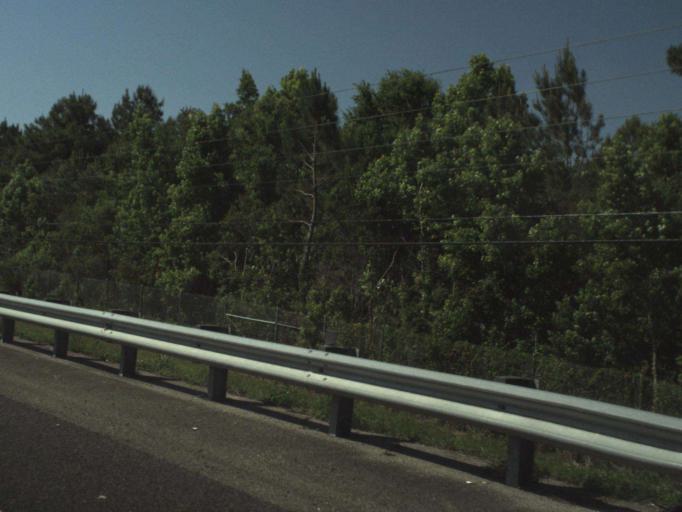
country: US
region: Florida
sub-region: Orange County
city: Christmas
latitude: 28.4344
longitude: -80.9652
